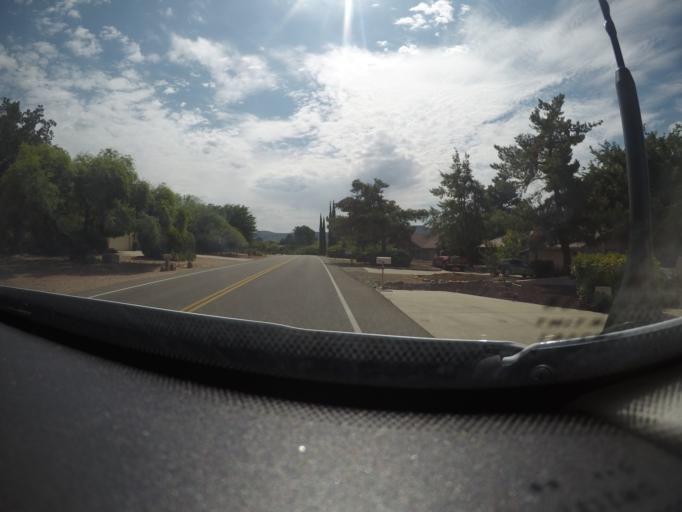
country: US
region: Arizona
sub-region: Yavapai County
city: Village of Oak Creek (Big Park)
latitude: 34.7871
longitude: -111.7696
